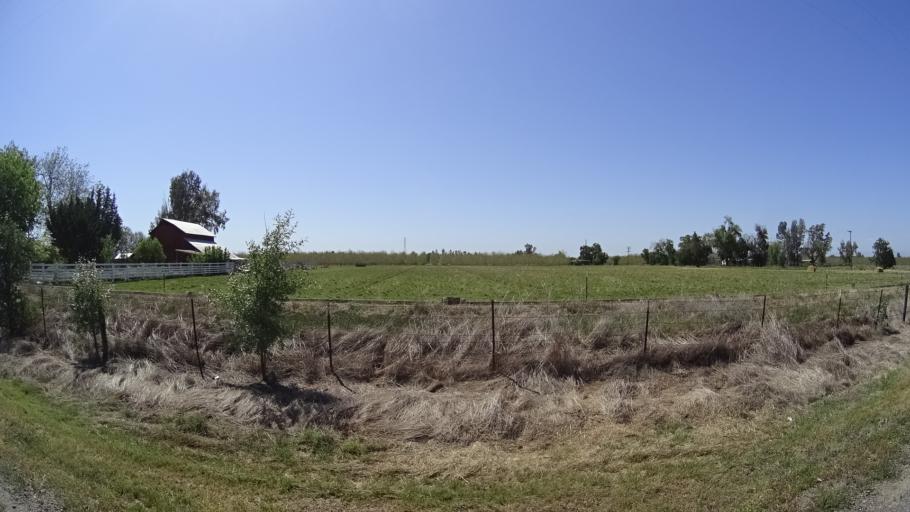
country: US
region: California
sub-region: Glenn County
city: Orland
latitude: 39.7978
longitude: -122.1580
